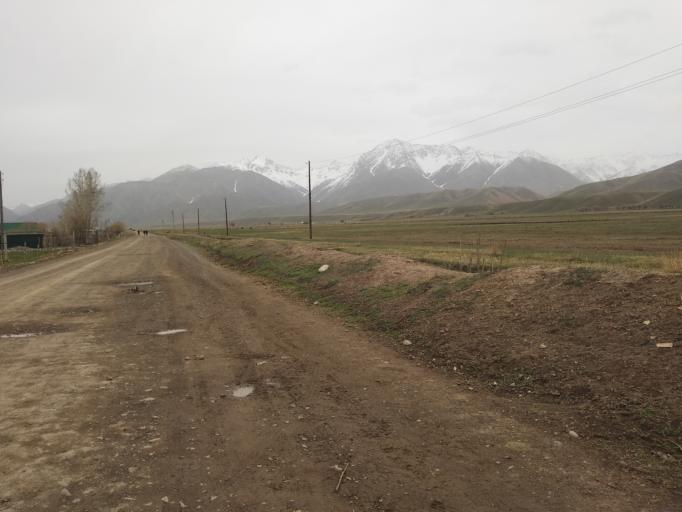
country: KG
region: Naryn
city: Naryn
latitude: 41.5164
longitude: 76.4404
